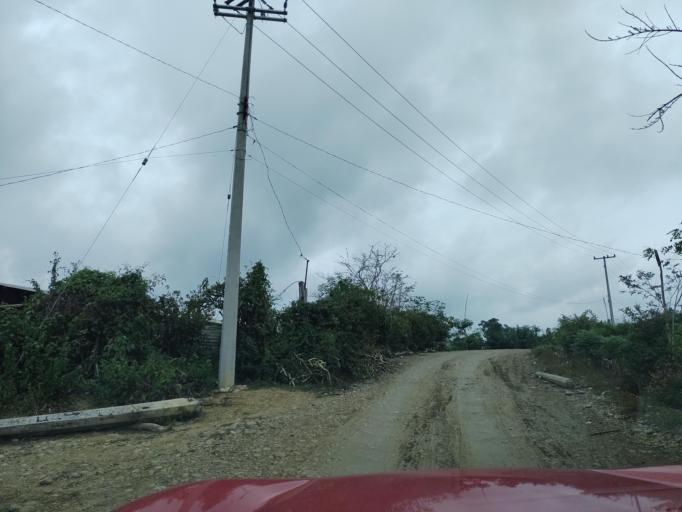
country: MX
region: Veracruz
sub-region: Coatzintla
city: Manuel Maria Contreras
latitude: 20.4088
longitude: -97.4569
